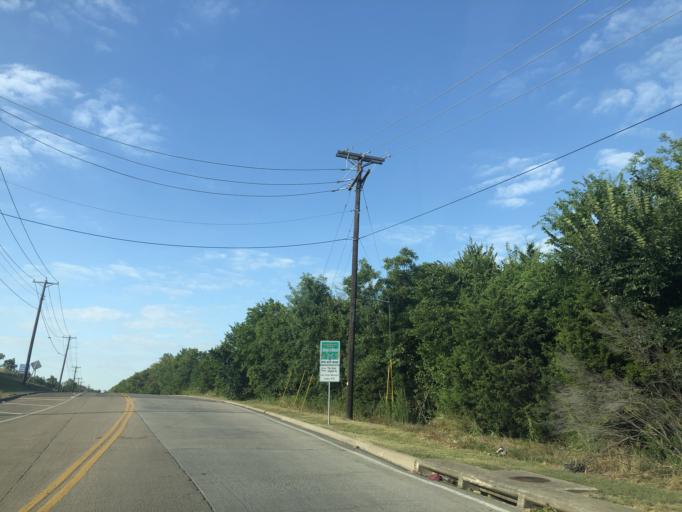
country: US
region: Texas
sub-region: Dallas County
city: Grand Prairie
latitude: 32.7491
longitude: -97.0287
